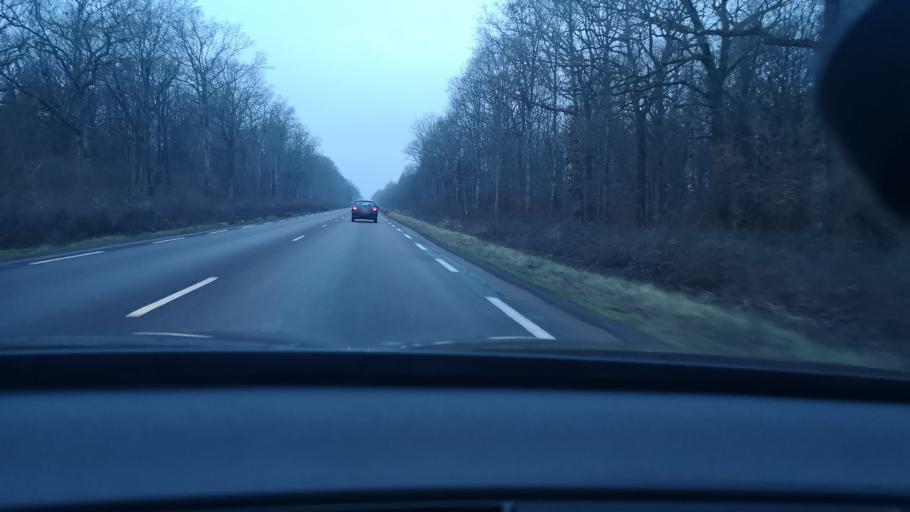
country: FR
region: Bourgogne
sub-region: Departement de la Cote-d'Or
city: Seurre
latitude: 47.0053
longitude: 5.0531
